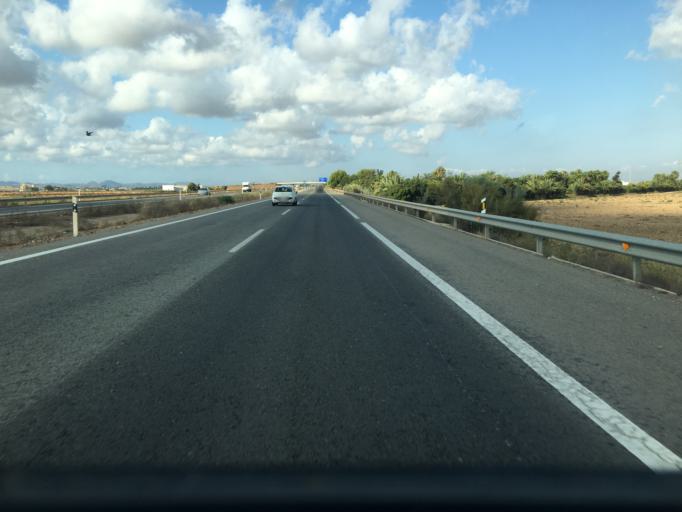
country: ES
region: Murcia
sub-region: Murcia
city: Los Alcazares
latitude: 37.7498
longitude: -0.8643
